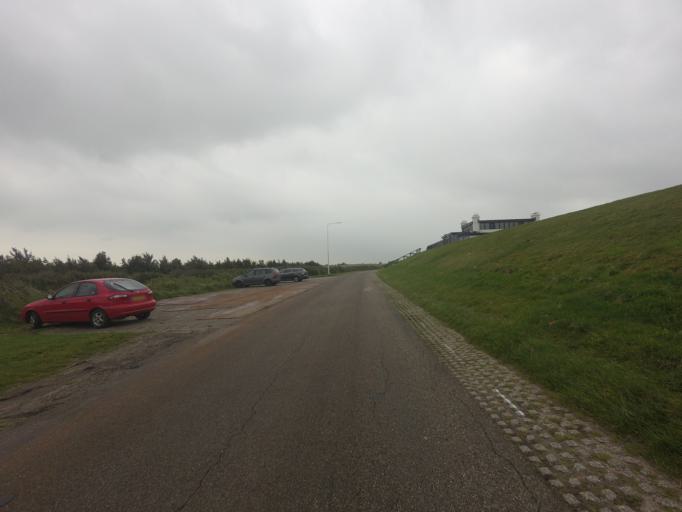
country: NL
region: Friesland
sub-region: Sudwest Fryslan
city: Koudum
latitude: 52.9338
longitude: 5.4041
